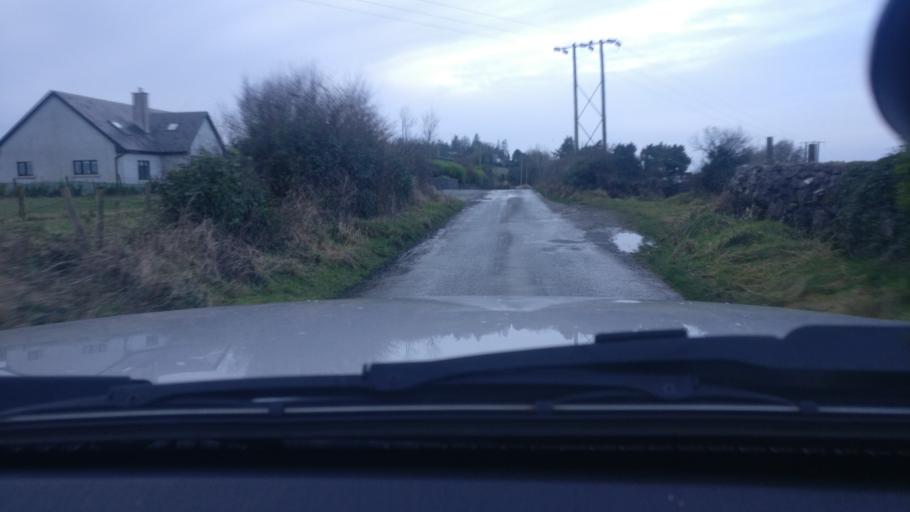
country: IE
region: Connaught
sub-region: County Galway
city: Loughrea
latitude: 53.1636
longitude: -8.5485
